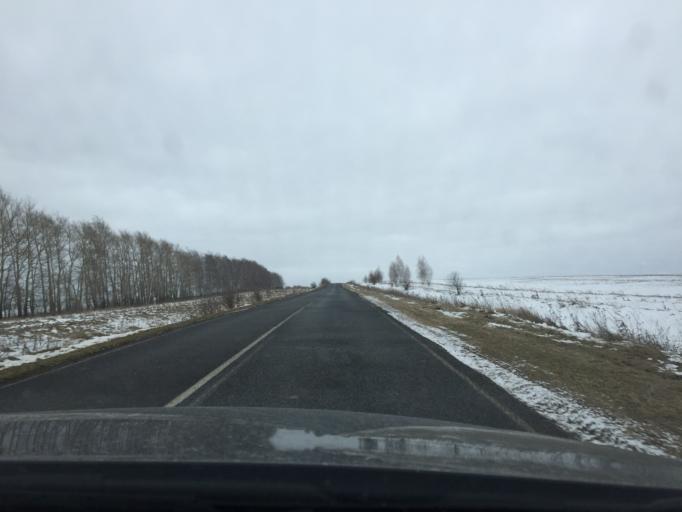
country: RU
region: Tula
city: Shchekino
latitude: 53.8286
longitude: 37.5131
